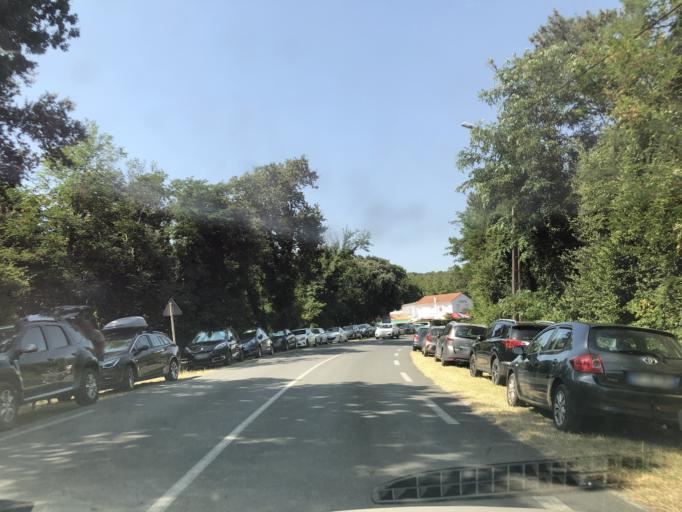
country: FR
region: Poitou-Charentes
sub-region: Departement de la Charente-Maritime
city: Meschers-sur-Gironde
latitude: 45.5673
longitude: -0.9712
